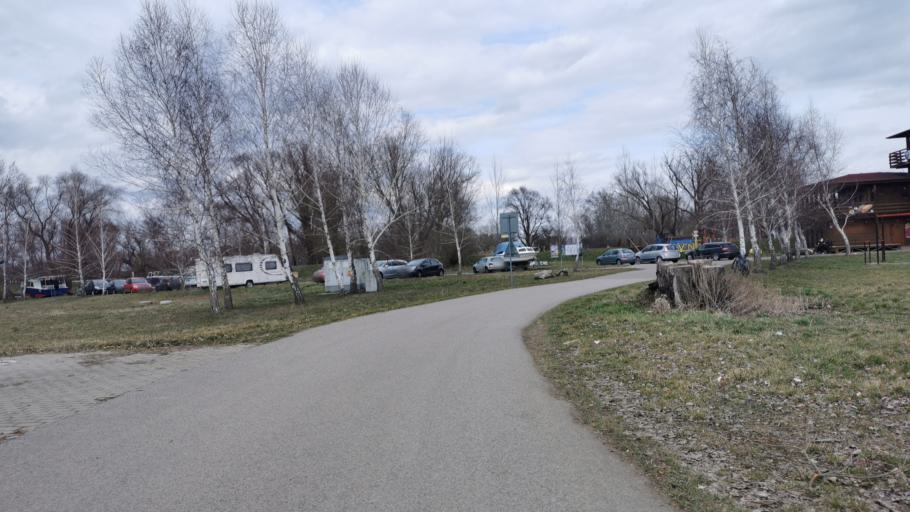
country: CZ
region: South Moravian
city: Rohatec
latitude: 48.8718
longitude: 17.2120
